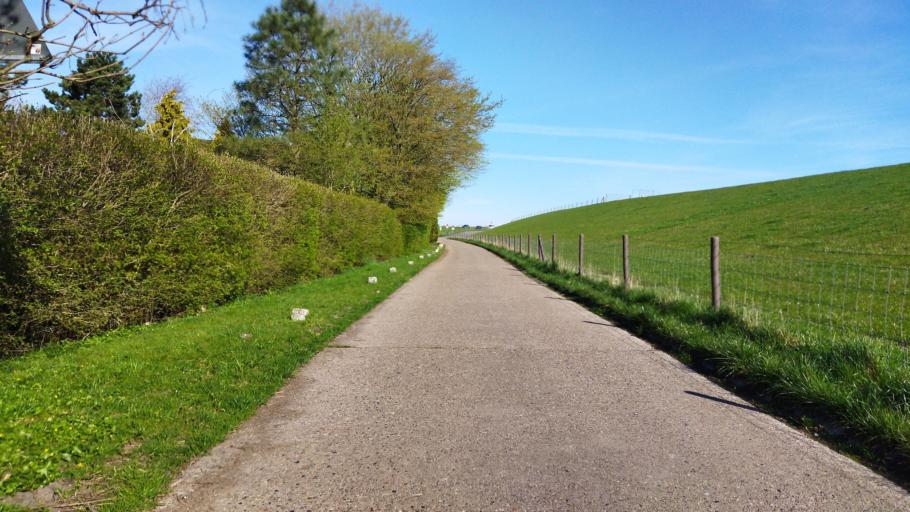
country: DE
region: Lower Saxony
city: Elsfleth
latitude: 53.2198
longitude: 8.4730
